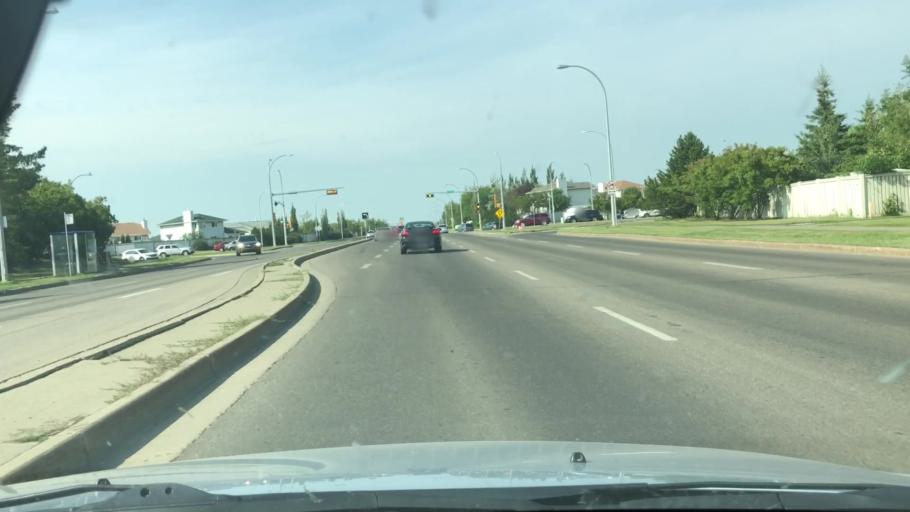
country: CA
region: Alberta
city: Edmonton
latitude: 53.6149
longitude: -113.4428
